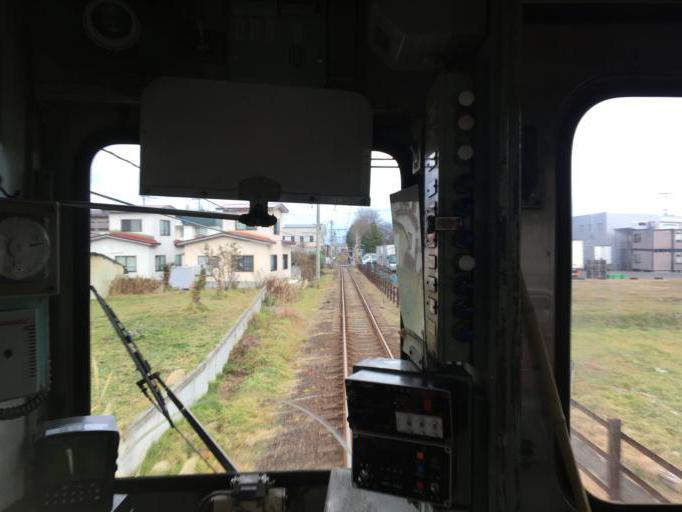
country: JP
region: Aomori
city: Hirosaki
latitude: 40.5758
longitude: 140.4731
